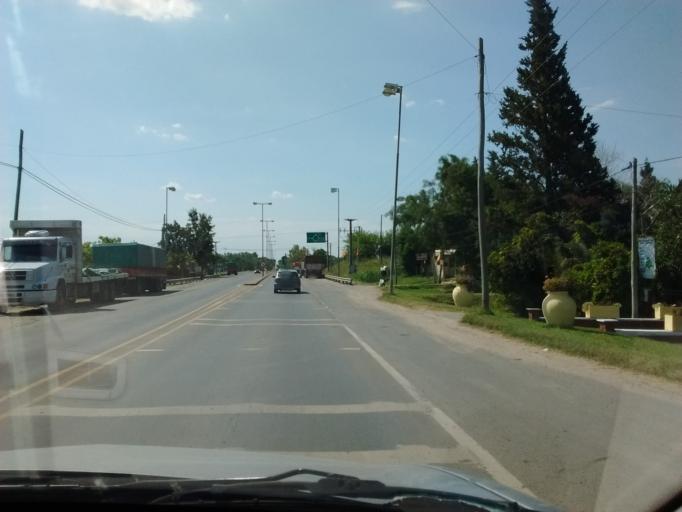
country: AR
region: Entre Rios
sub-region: Departamento de Victoria
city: Victoria
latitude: -32.6076
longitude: -60.1668
